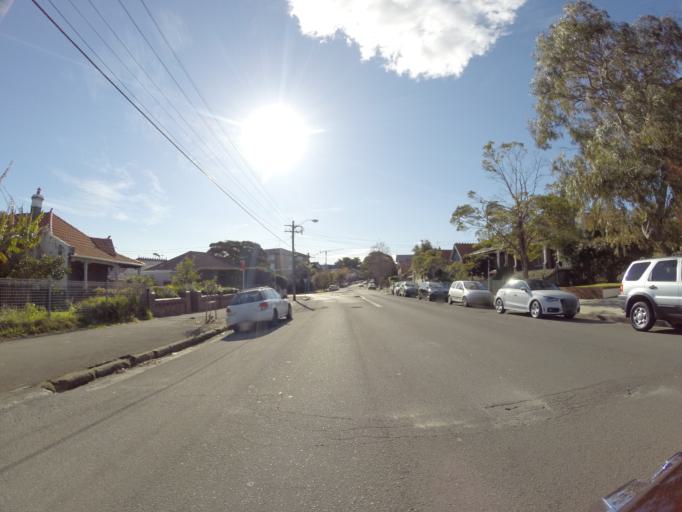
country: AU
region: New South Wales
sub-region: Randwick
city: Randwick
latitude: -33.9223
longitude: 151.2435
